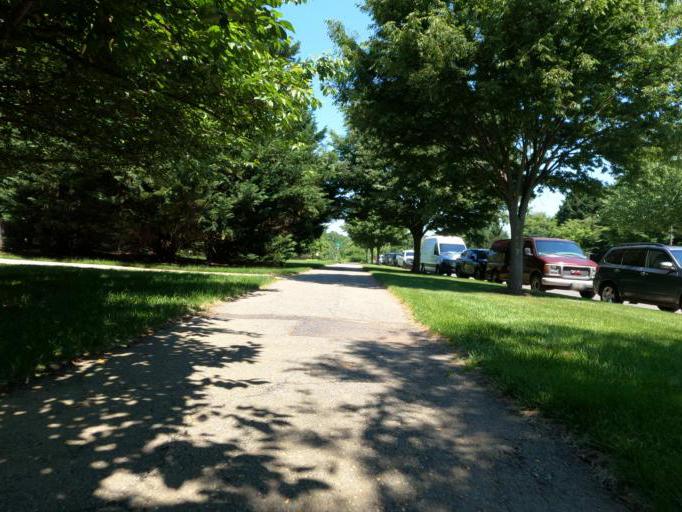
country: US
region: Maryland
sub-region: Montgomery County
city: Germantown
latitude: 39.2063
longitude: -77.2658
